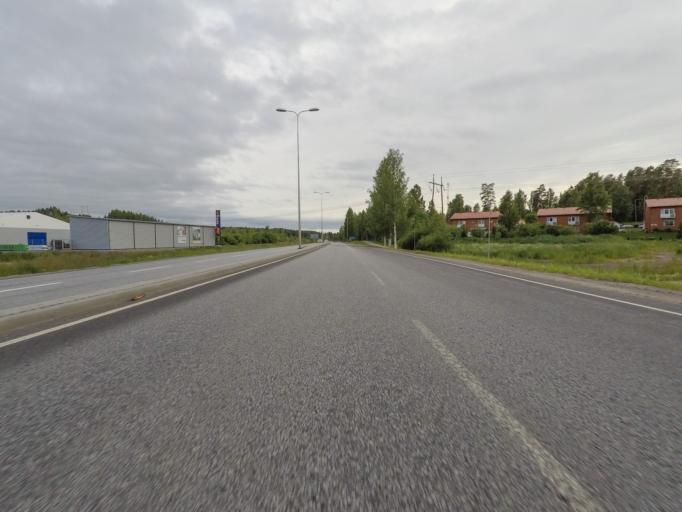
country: FI
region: Southern Savonia
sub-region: Savonlinna
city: Savonlinna
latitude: 61.8742
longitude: 28.9519
